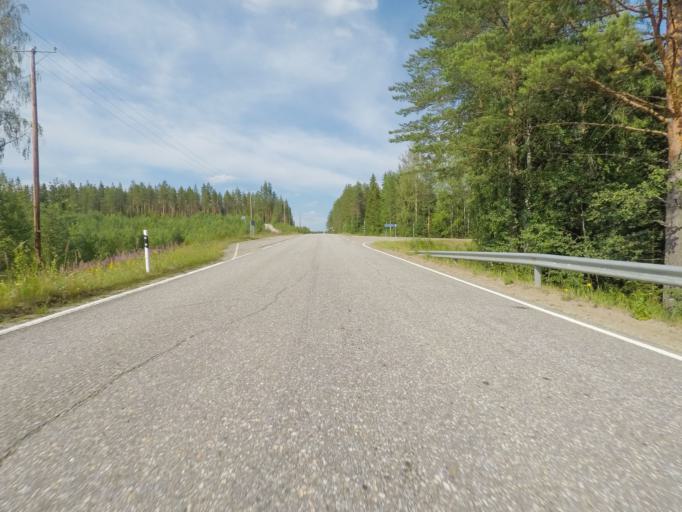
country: FI
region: Southern Savonia
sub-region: Savonlinna
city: Sulkava
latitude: 61.7828
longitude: 28.2399
